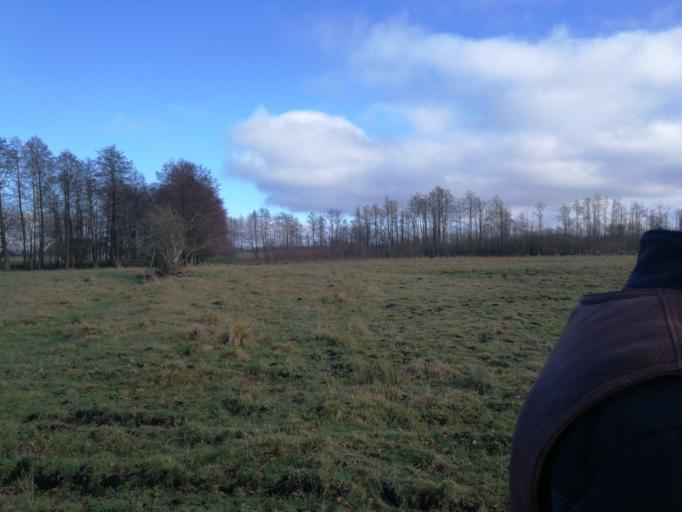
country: PL
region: Warmian-Masurian Voivodeship
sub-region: Powiat dzialdowski
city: Rybno
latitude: 53.4123
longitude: 19.9085
